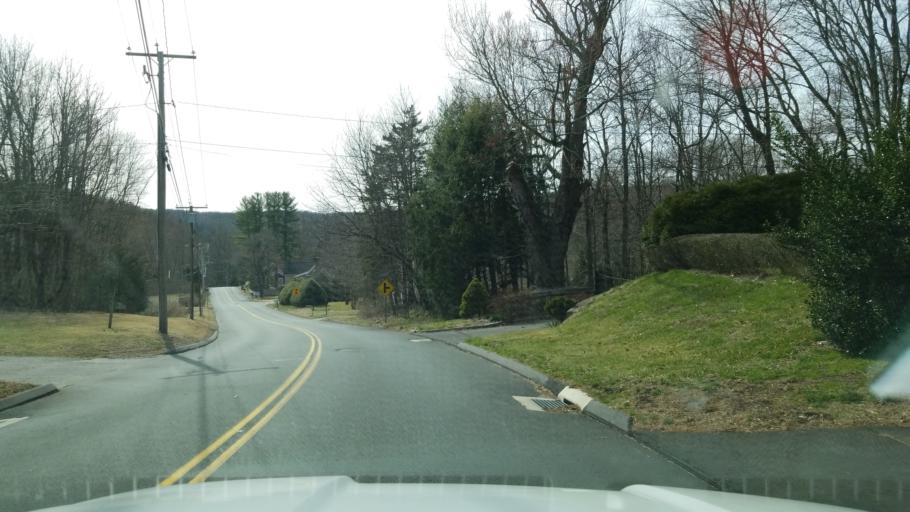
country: US
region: Connecticut
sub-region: Hartford County
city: Glastonbury Center
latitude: 41.6661
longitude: -72.5804
